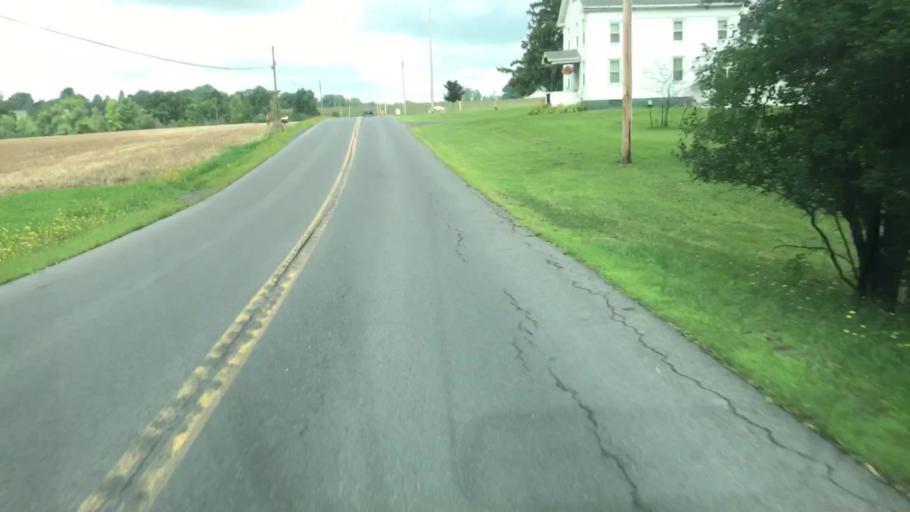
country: US
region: New York
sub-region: Cayuga County
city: Melrose Park
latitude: 42.9182
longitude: -76.5219
